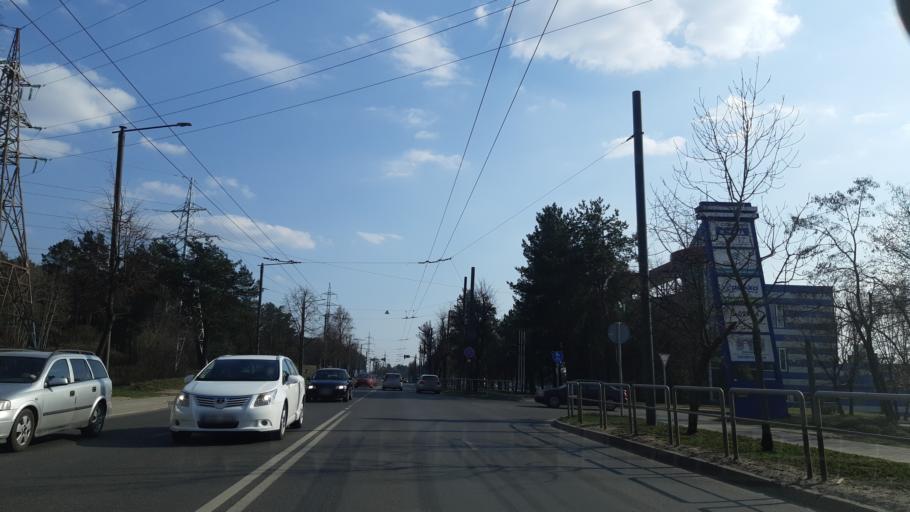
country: LT
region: Kauno apskritis
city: Dainava (Kaunas)
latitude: 54.8881
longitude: 24.0055
